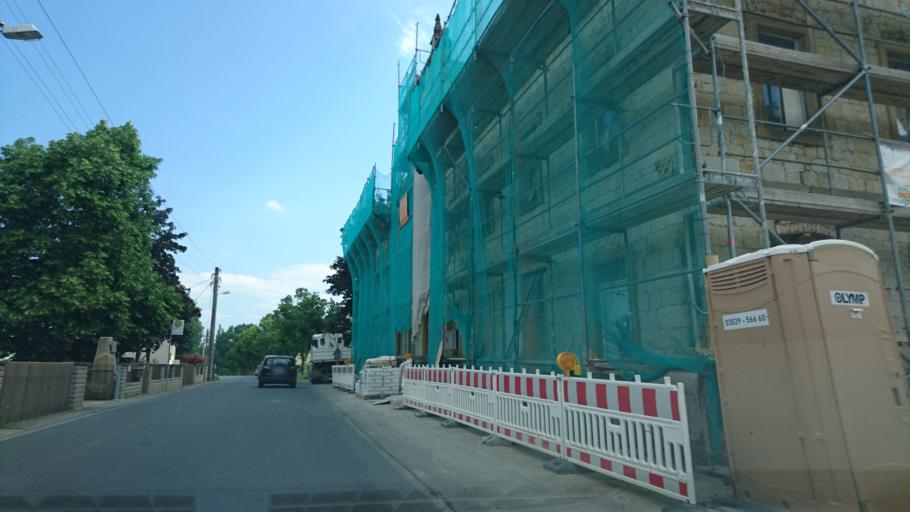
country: DE
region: Saxony
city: Dohma
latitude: 50.9021
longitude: 13.9621
